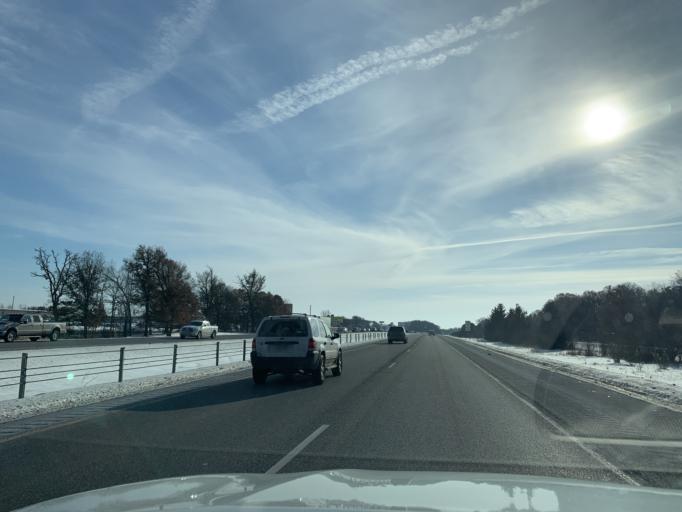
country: US
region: Minnesota
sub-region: Chisago County
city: Wyoming
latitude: 45.3291
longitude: -93.0046
